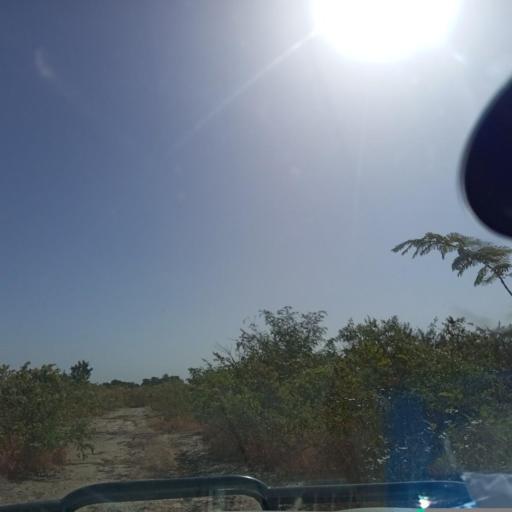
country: ML
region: Koulikoro
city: Koulikoro
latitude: 12.6845
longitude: -7.3037
